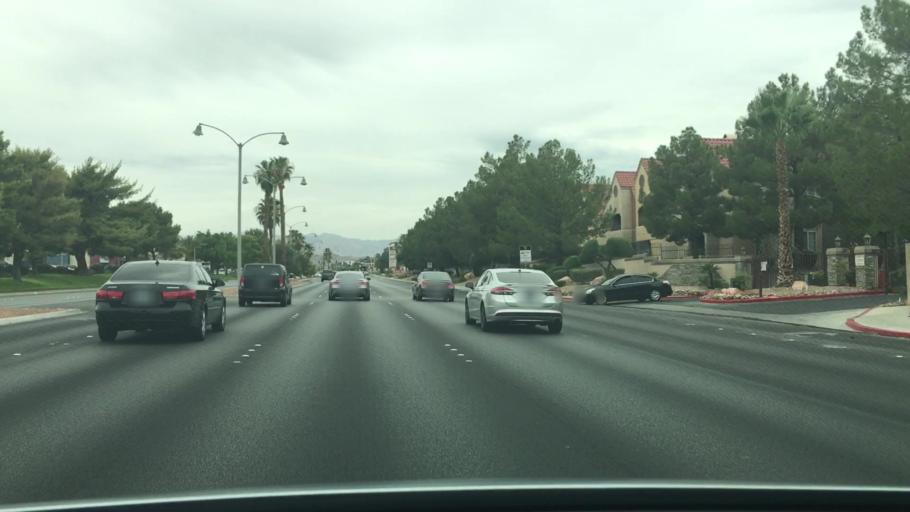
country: US
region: Nevada
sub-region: Clark County
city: Summerlin South
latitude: 36.1443
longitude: -115.2926
